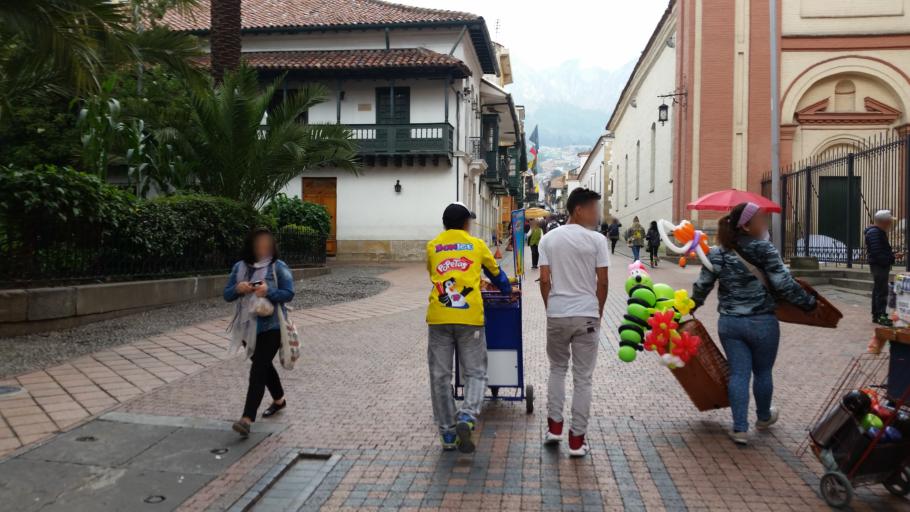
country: CO
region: Bogota D.C.
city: Bogota
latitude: 4.5971
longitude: -74.0755
